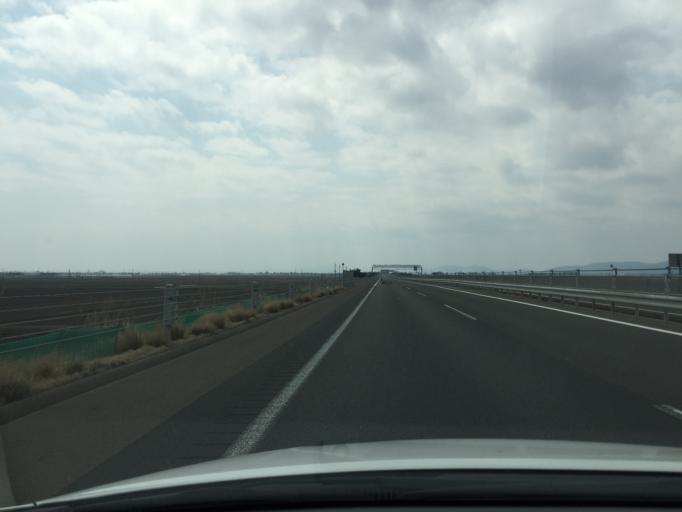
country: JP
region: Miyagi
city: Iwanuma
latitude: 38.1528
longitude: 140.8960
